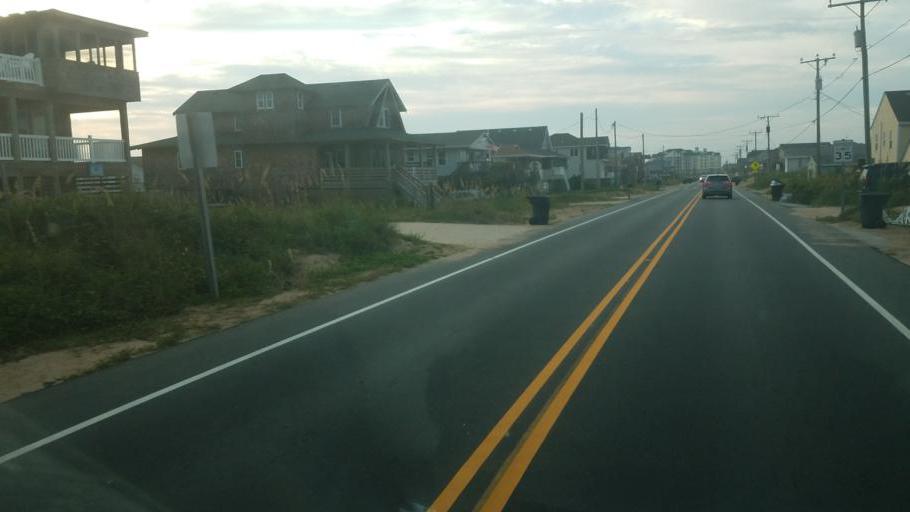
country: US
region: North Carolina
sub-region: Dare County
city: Kitty Hawk
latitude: 36.0951
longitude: -75.7080
